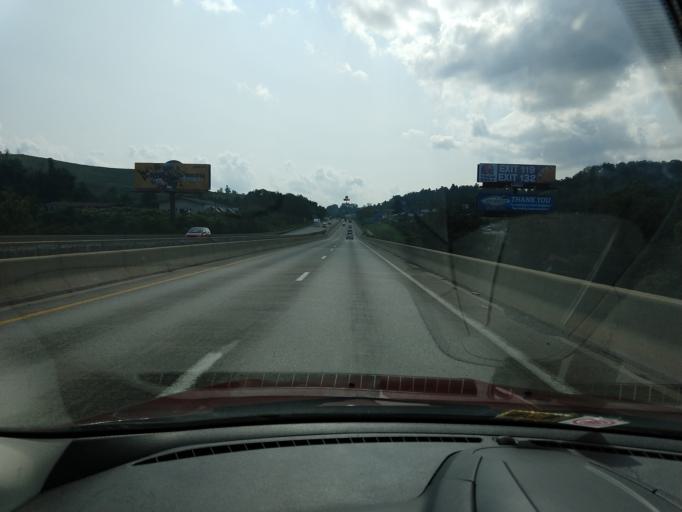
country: US
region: West Virginia
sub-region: Marion County
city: Pleasant Valley
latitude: 39.4396
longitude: -80.1750
